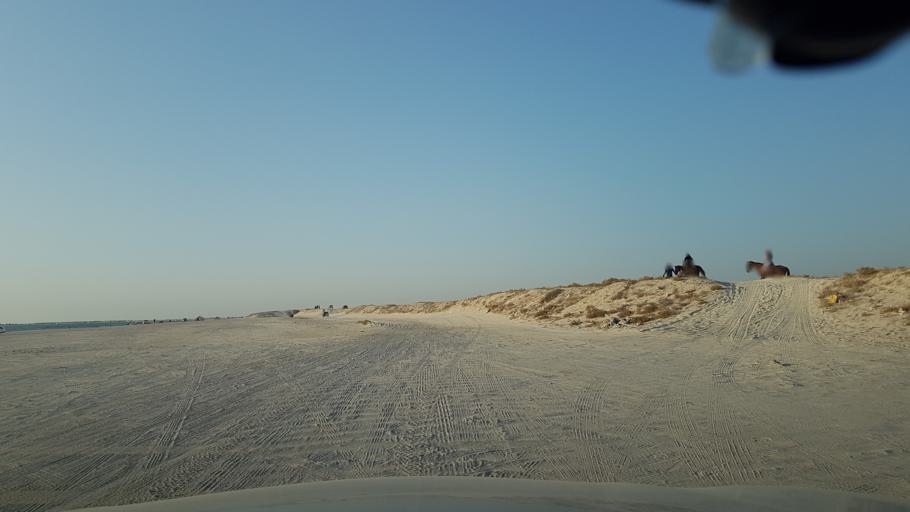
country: BH
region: Manama
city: Jidd Hafs
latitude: 26.2413
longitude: 50.5030
